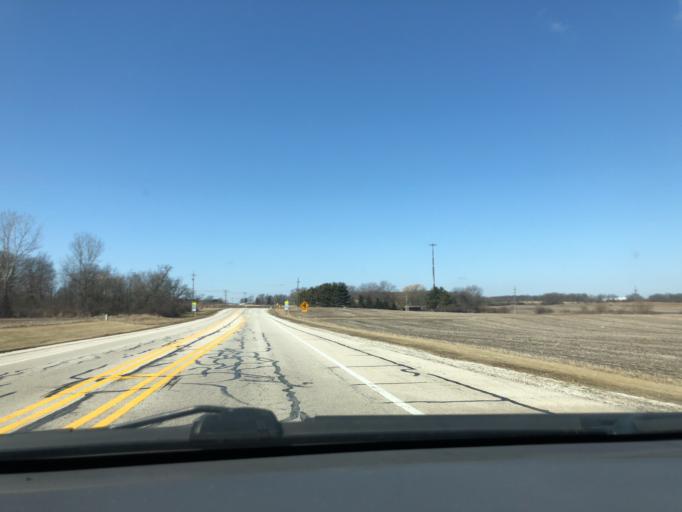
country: US
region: Illinois
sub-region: Kane County
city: Hampshire
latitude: 42.1227
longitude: -88.4876
